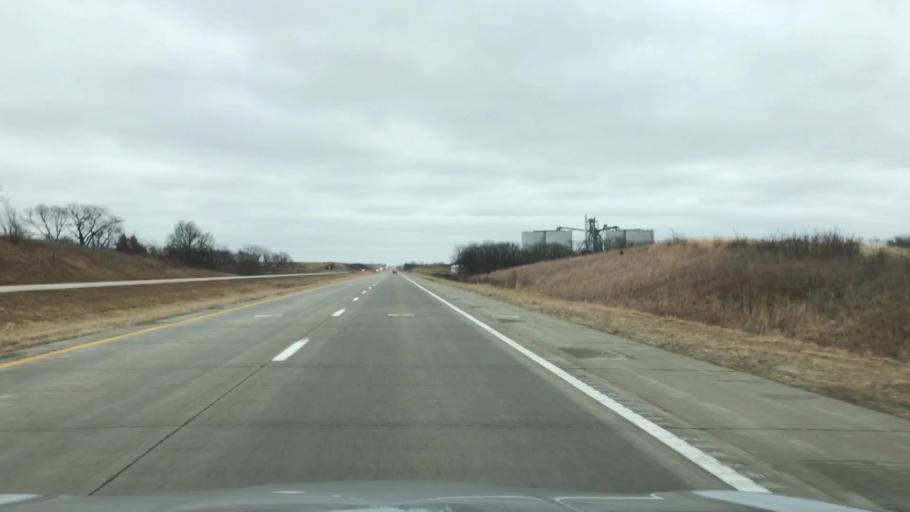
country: US
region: Missouri
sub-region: Caldwell County
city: Hamilton
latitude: 39.7353
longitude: -93.9157
